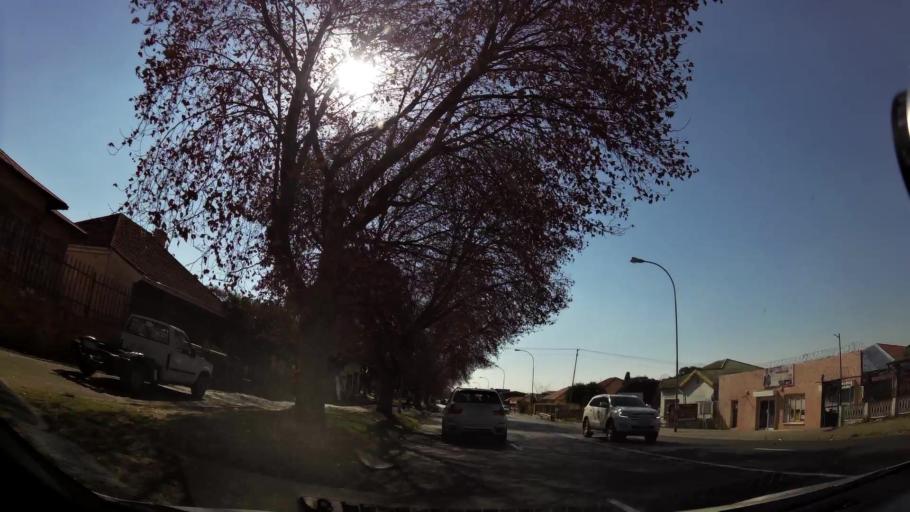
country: ZA
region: Gauteng
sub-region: City of Johannesburg Metropolitan Municipality
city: Johannesburg
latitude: -26.2504
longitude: 28.0552
